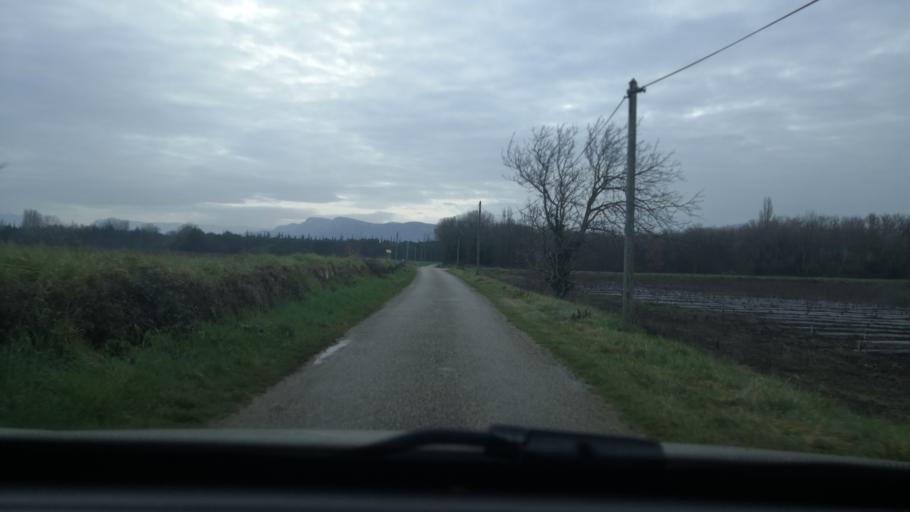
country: FR
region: Rhone-Alpes
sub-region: Departement de la Drome
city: La Begude-de-Mazenc
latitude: 44.5657
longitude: 4.8762
